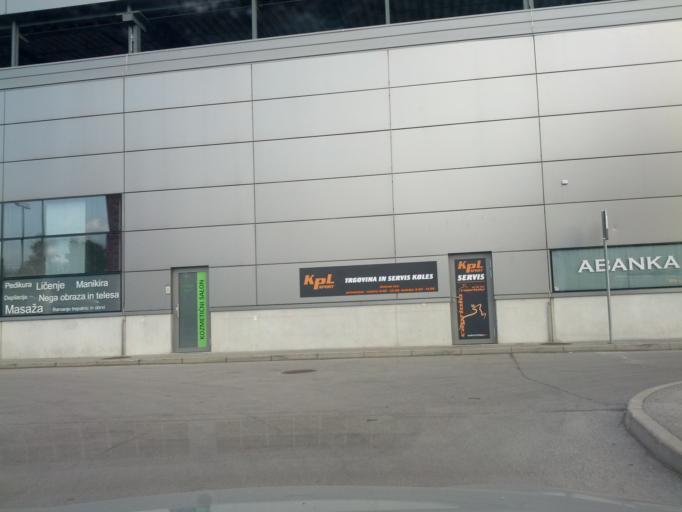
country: SI
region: Ljubljana
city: Ljubljana
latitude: 46.0678
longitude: 14.5356
